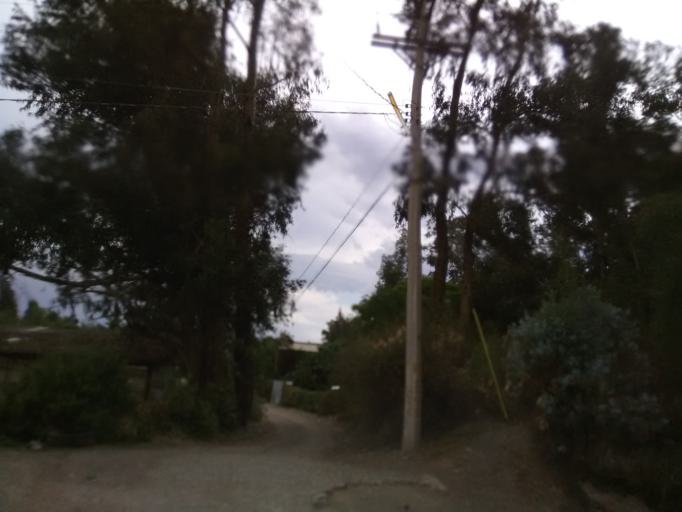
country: BO
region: Cochabamba
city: Cochabamba
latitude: -17.3565
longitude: -66.2171
